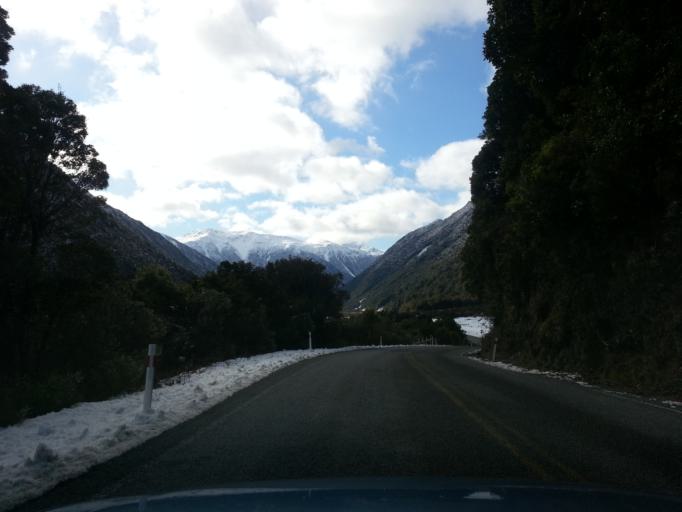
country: NZ
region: West Coast
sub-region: Grey District
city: Greymouth
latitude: -42.8557
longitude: 171.5593
